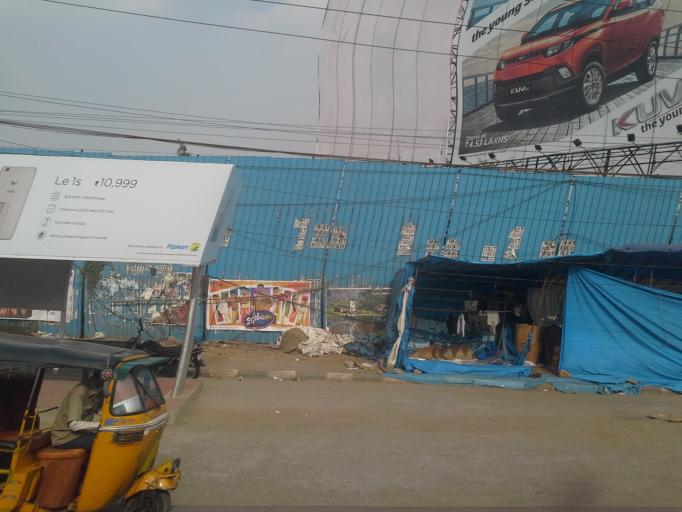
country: IN
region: Telangana
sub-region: Rangareddi
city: Kukatpalli
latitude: 17.4557
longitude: 78.3778
